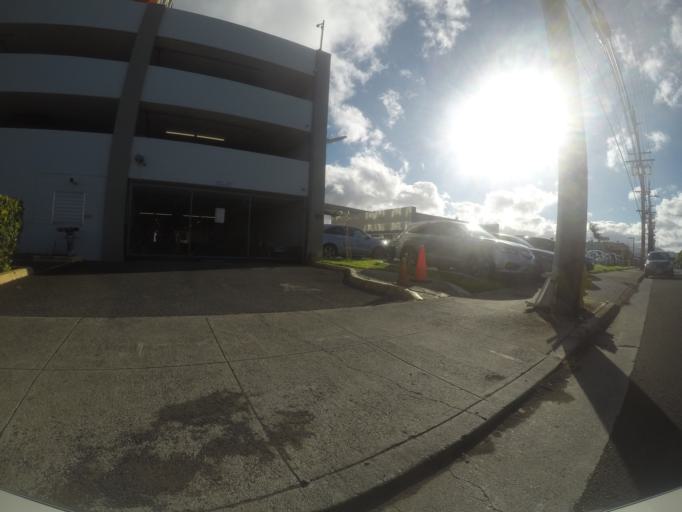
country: US
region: Hawaii
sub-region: Honolulu County
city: Halawa Heights
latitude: 21.3358
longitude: -157.9131
